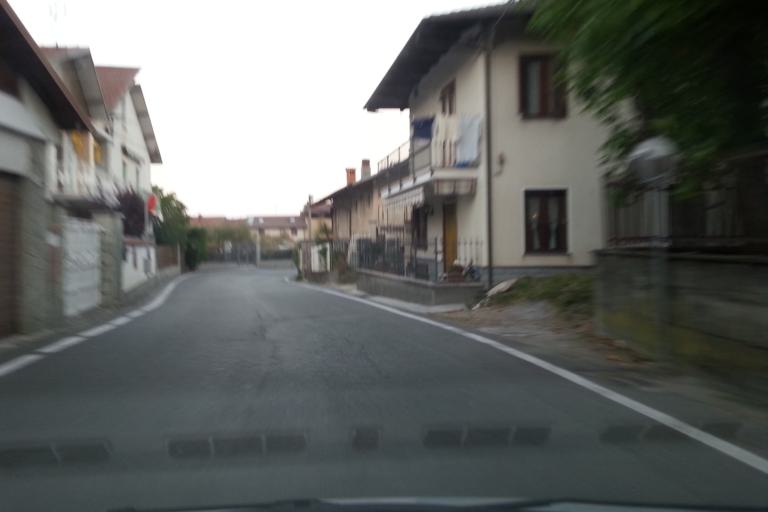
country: IT
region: Piedmont
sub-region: Provincia di Torino
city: Giaveno
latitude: 45.0438
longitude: 7.3327
